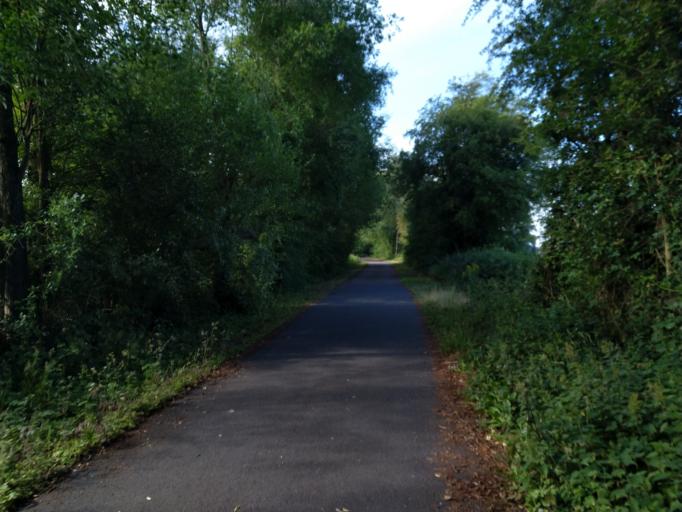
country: BE
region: Wallonia
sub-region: Province du Hainaut
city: Erquelinnes
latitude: 50.3380
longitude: 4.1007
